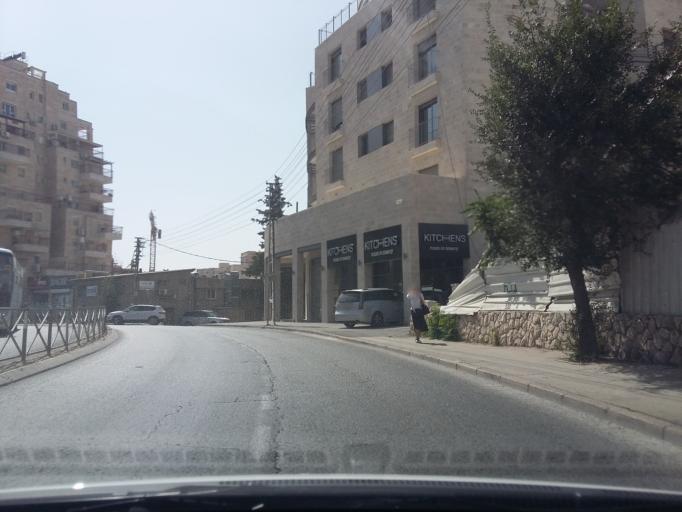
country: IL
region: Jerusalem
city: West Jerusalem
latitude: 31.7925
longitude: 35.2050
